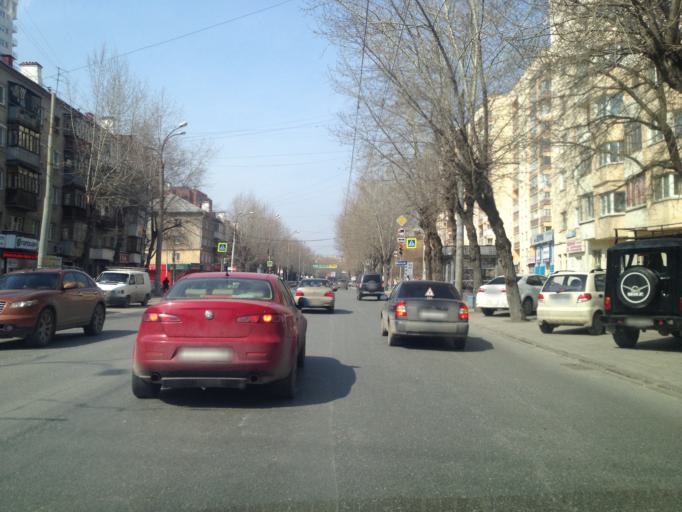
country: RU
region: Sverdlovsk
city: Yekaterinburg
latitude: 56.8023
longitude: 60.6284
